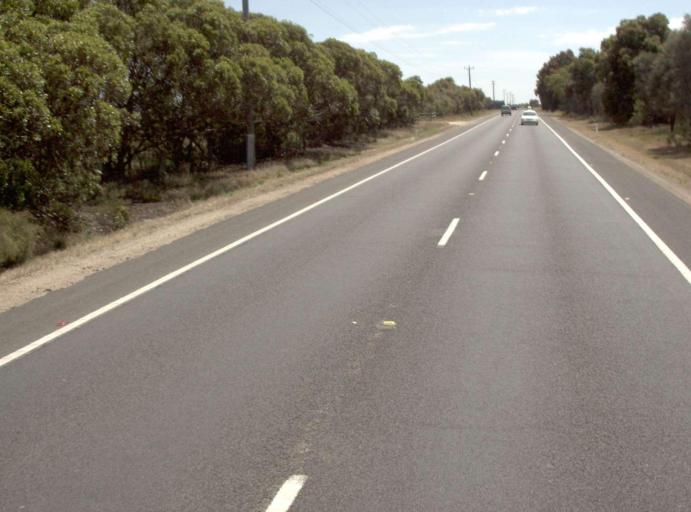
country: AU
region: Victoria
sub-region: Wellington
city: Sale
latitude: -38.1000
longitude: 146.9670
